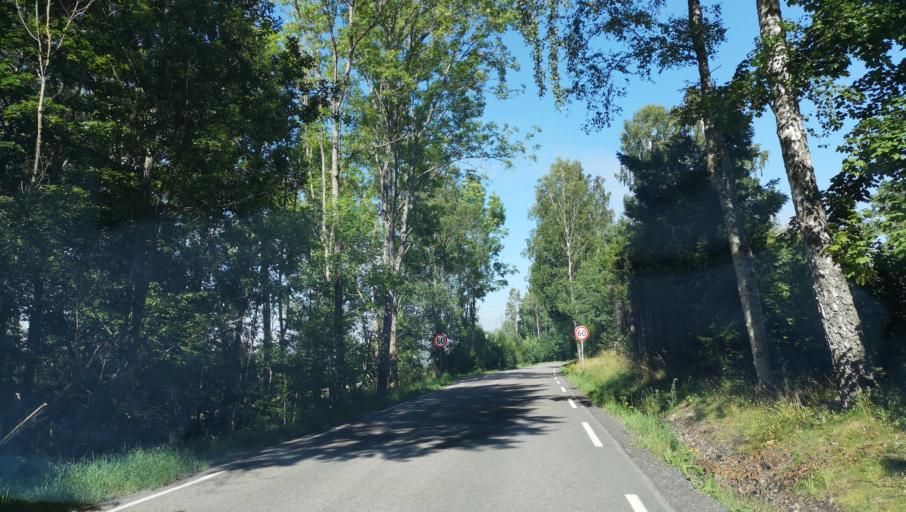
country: NO
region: Akershus
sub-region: Vestby
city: Vestby
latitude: 59.5389
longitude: 10.6906
